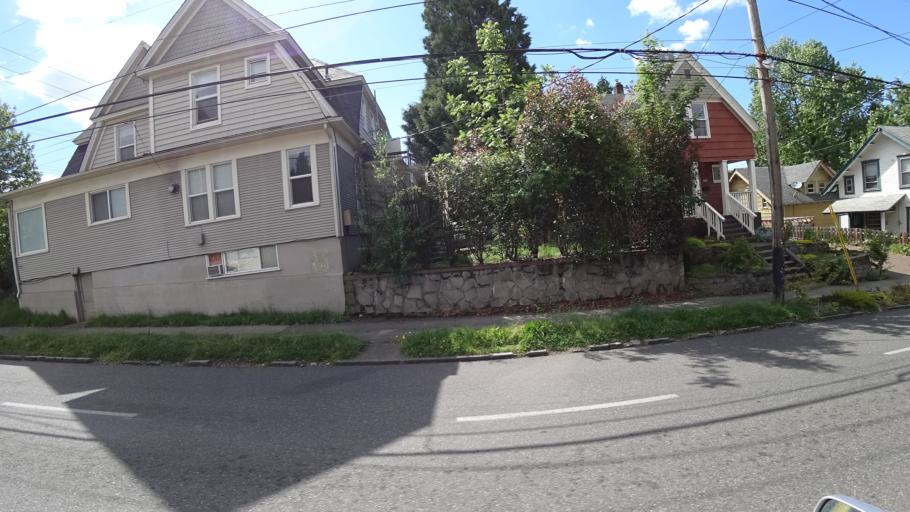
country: US
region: Oregon
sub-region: Multnomah County
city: Portland
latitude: 45.5196
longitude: -122.6455
